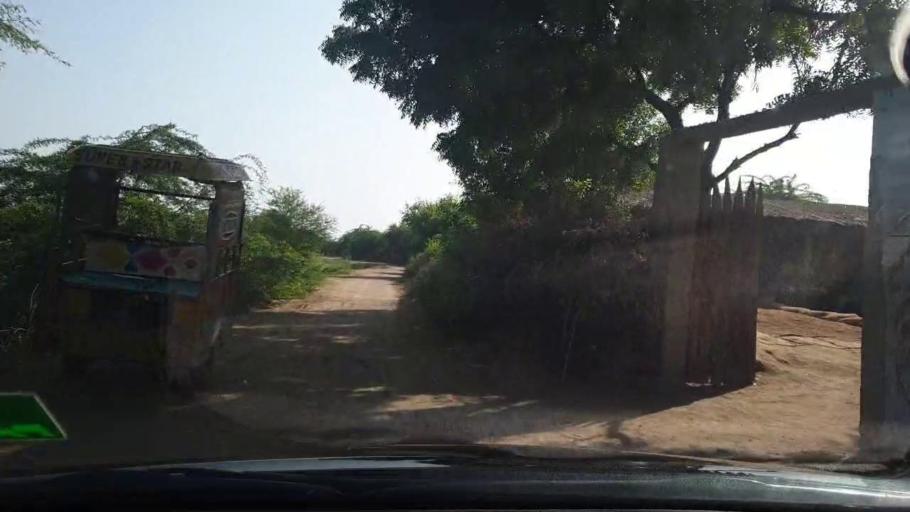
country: PK
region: Sindh
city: Tando Bago
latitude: 24.7209
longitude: 68.9948
